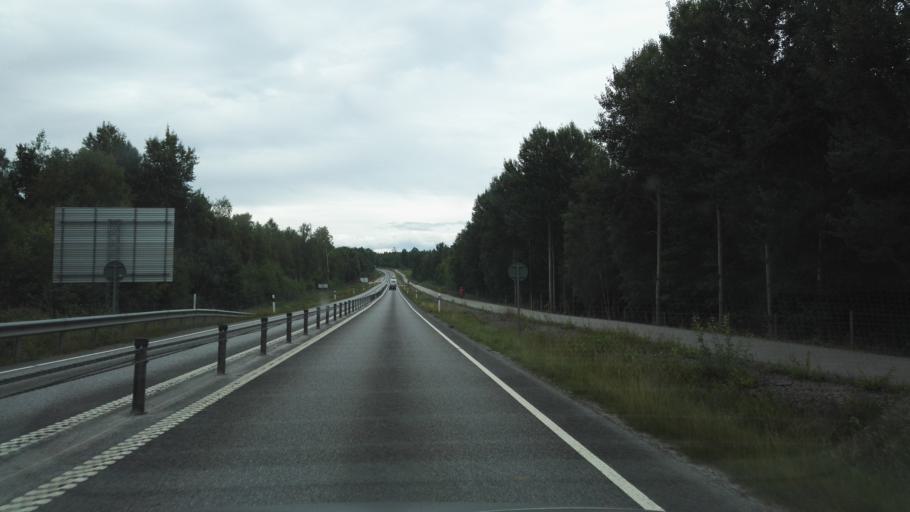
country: SE
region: Kronoberg
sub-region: Vaxjo Kommun
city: Vaexjoe
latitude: 56.9253
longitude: 14.8612
